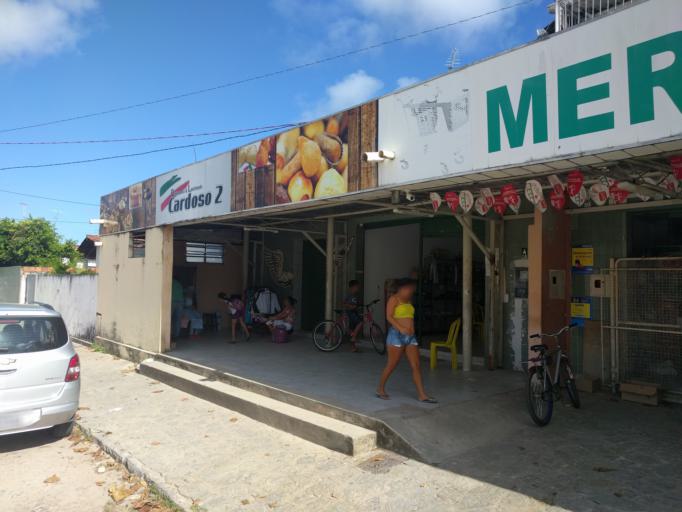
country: BR
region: Paraiba
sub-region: Joao Pessoa
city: Joao Pessoa
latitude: -7.1668
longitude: -34.8303
